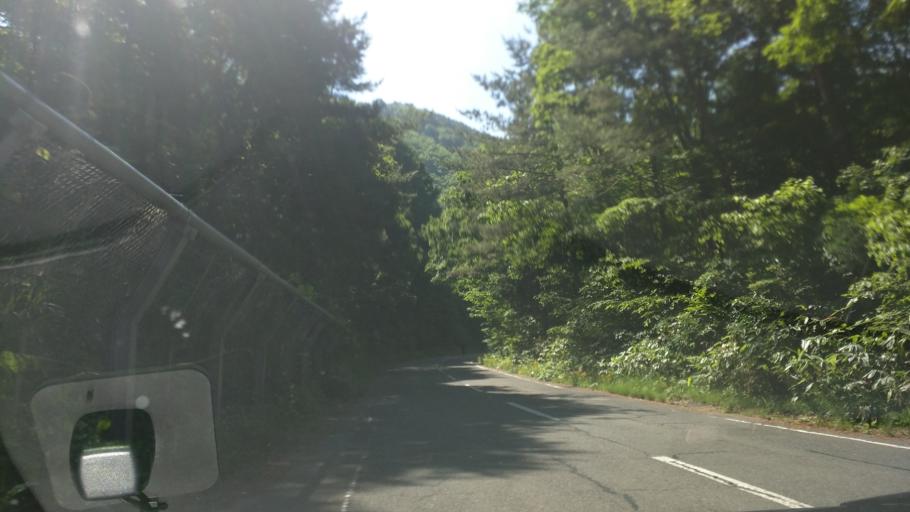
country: JP
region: Fukushima
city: Kitakata
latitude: 37.3870
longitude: 139.8763
